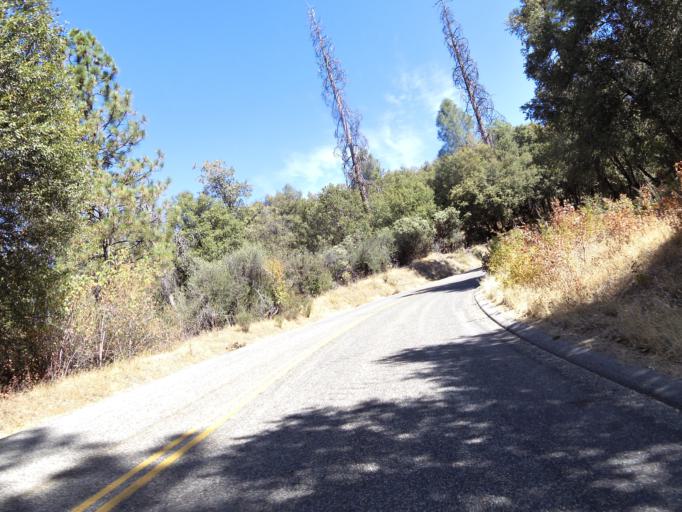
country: US
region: California
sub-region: Madera County
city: Oakhurst
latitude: 37.3851
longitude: -119.6093
